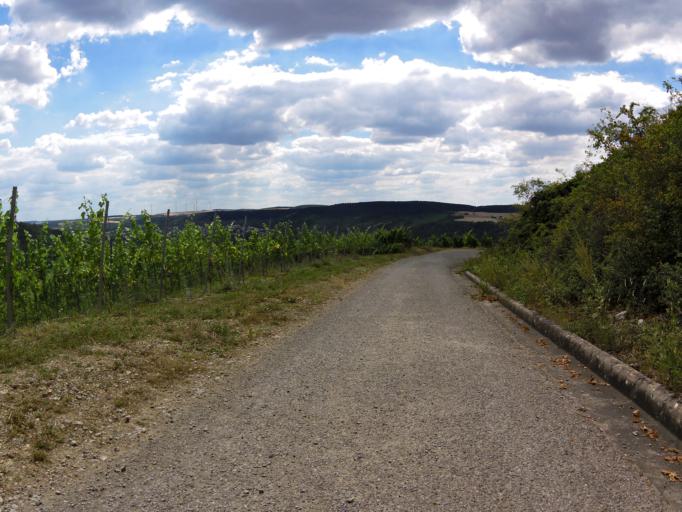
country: DE
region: Bavaria
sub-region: Regierungsbezirk Unterfranken
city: Thungersheim
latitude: 49.8834
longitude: 9.8593
